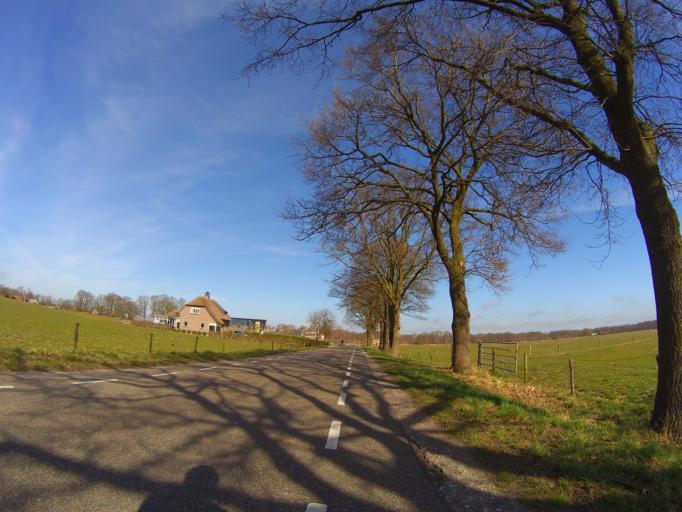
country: NL
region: Utrecht
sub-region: Gemeente Veenendaal
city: Veenendaal
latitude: 52.0459
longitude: 5.5395
